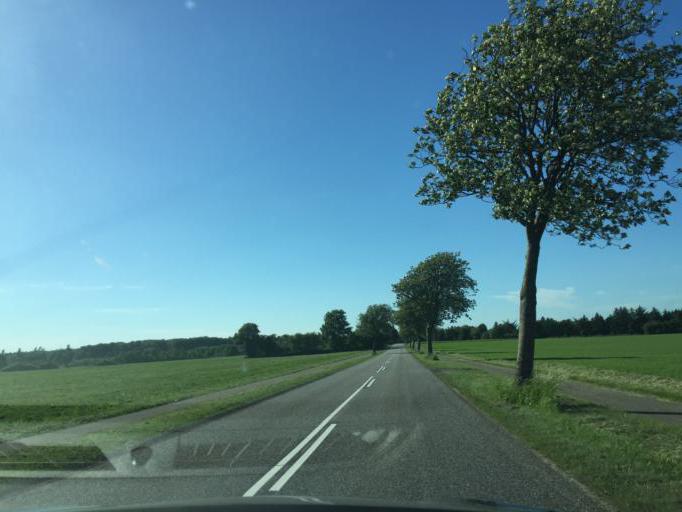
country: DK
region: Zealand
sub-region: Koge Kommune
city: Bjaeverskov
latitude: 55.4305
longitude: 11.9790
